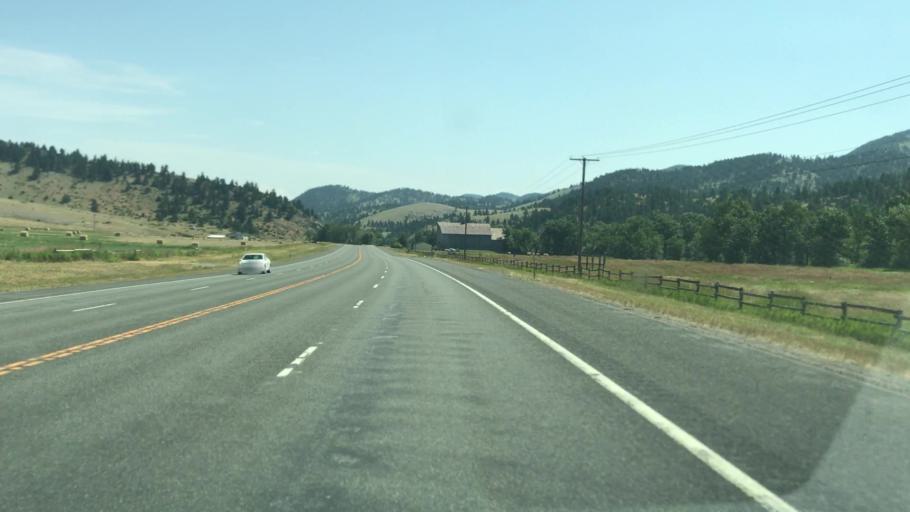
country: US
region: Montana
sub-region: Lewis and Clark County
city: Helena West Side
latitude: 46.5761
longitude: -112.1627
